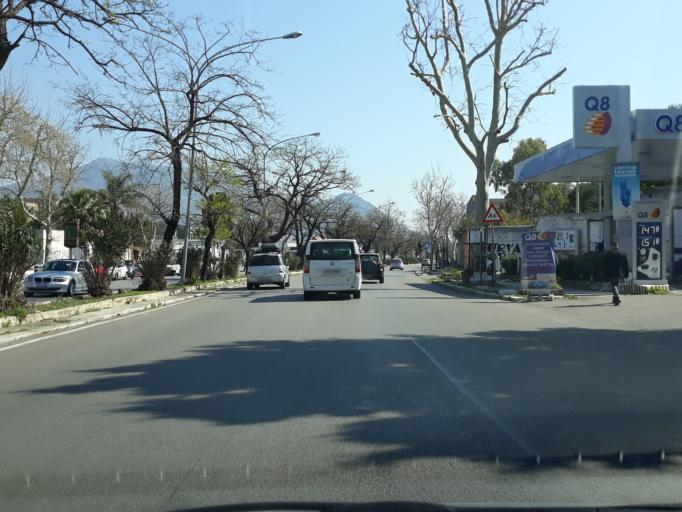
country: IT
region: Sicily
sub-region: Palermo
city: Palermo
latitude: 38.1363
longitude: 13.3169
